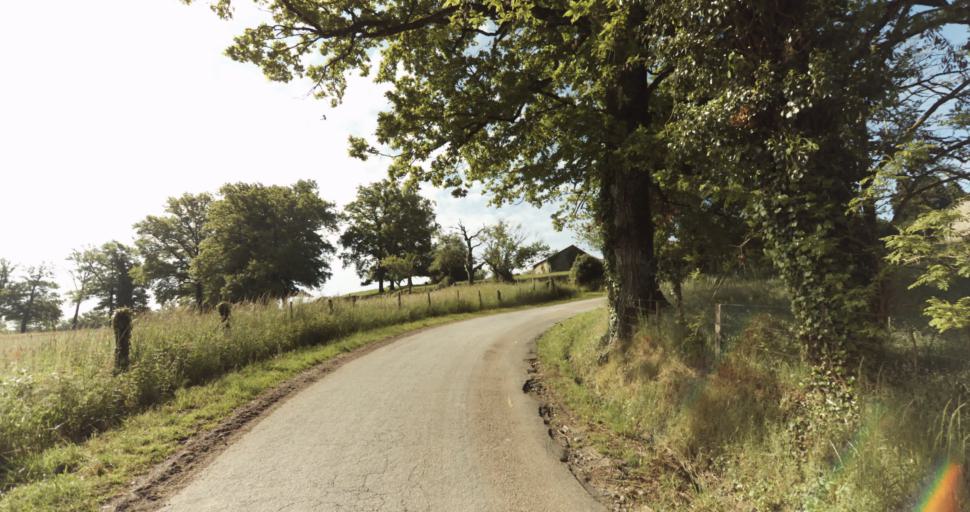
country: FR
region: Limousin
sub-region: Departement de la Haute-Vienne
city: Solignac
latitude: 45.7071
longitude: 1.2643
